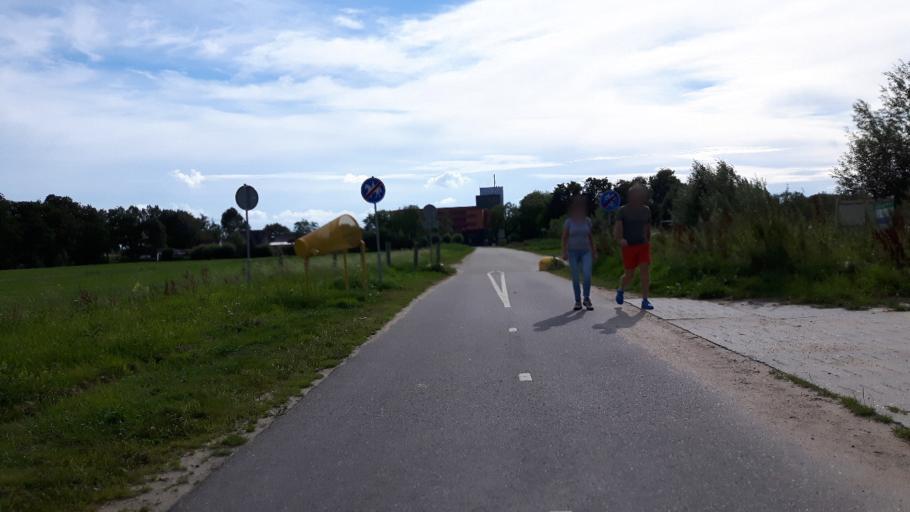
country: NL
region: Utrecht
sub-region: Gemeente Woerden
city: Woerden
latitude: 52.0789
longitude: 4.9178
